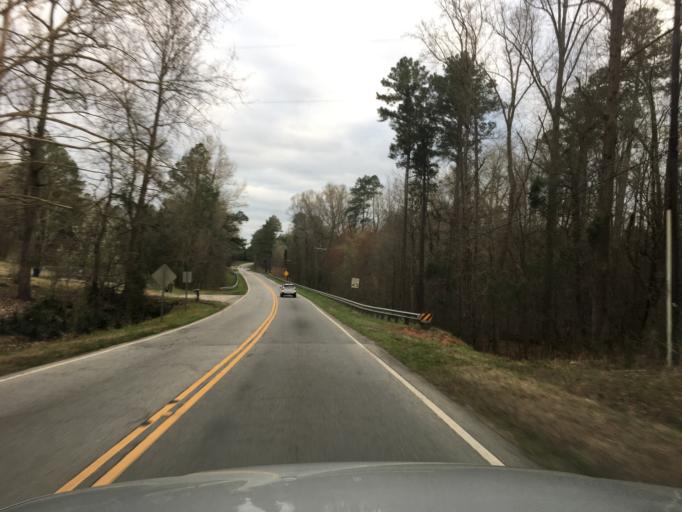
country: US
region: South Carolina
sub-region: Saluda County
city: Saluda
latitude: 33.9892
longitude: -81.7709
